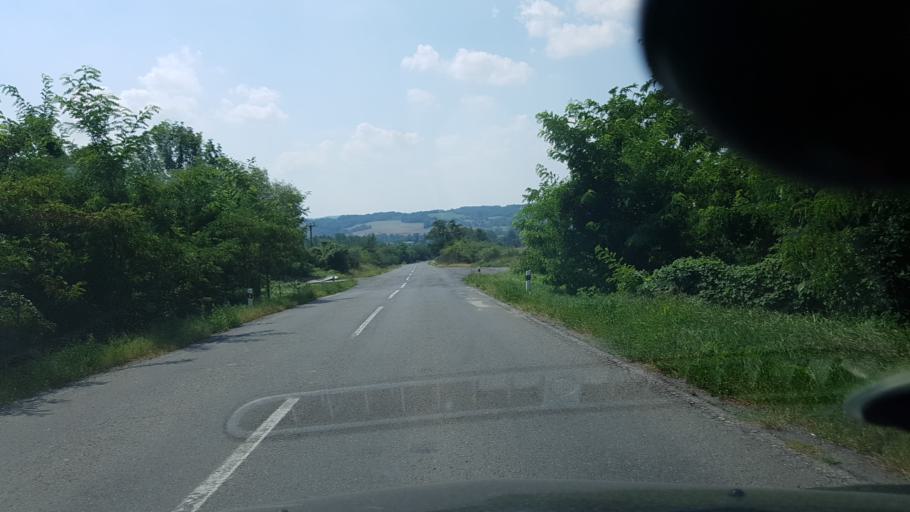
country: SK
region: Banskobystricky
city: Velky Krtis
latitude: 48.2435
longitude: 19.4301
